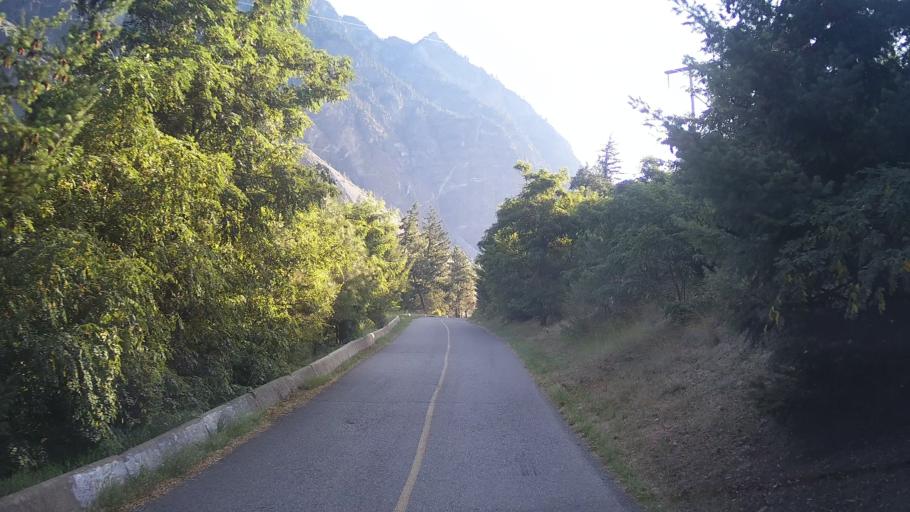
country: CA
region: British Columbia
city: Lillooet
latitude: 50.6656
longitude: -121.9897
